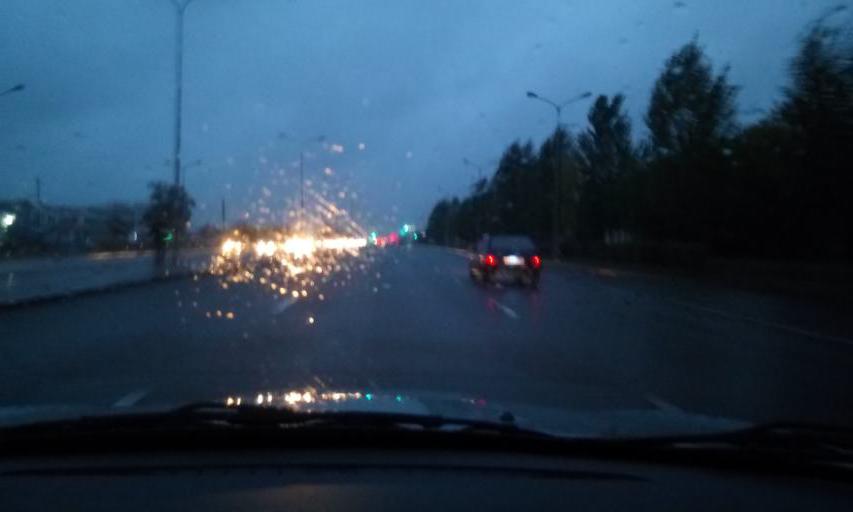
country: KZ
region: Astana Qalasy
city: Astana
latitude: 51.1894
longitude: 71.3411
